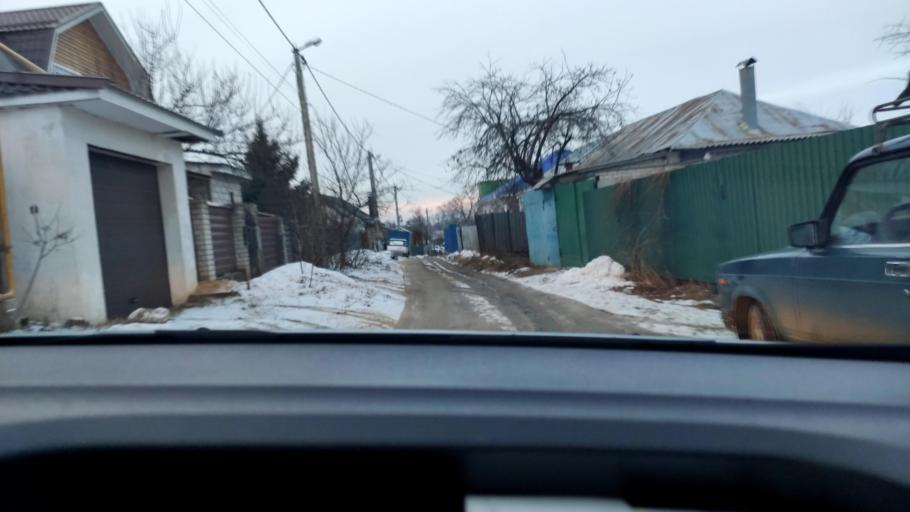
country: RU
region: Voronezj
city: Podgornoye
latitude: 51.7334
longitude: 39.1467
